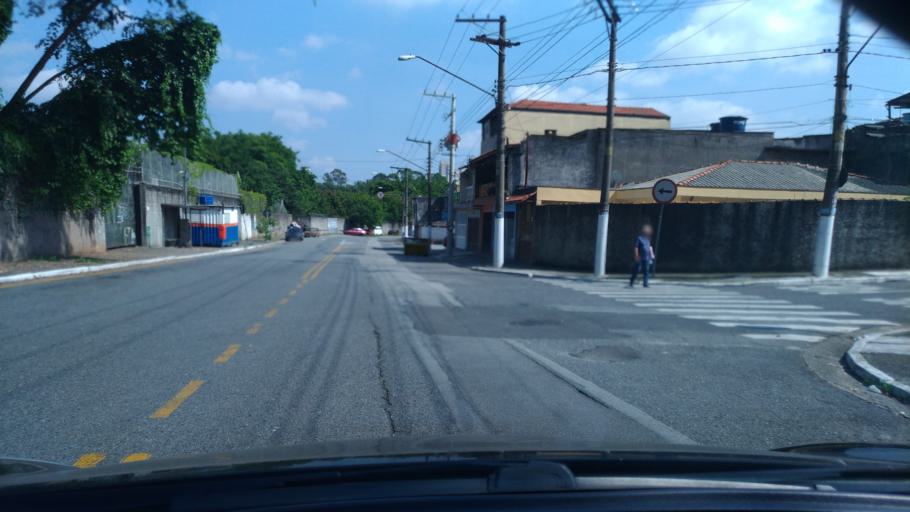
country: BR
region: Sao Paulo
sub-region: Sao Bernardo Do Campo
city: Sao Bernardo do Campo
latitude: -23.6975
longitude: -46.5834
